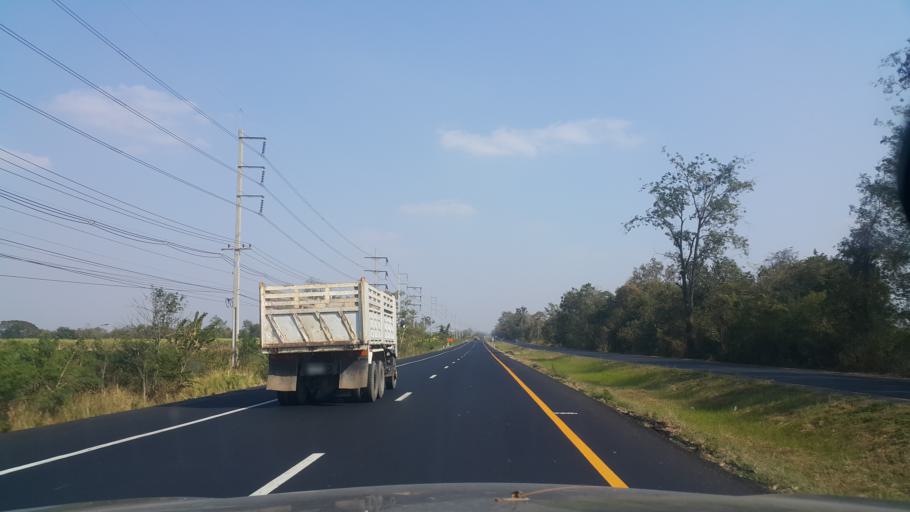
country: TH
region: Nakhon Ratchasima
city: Nong Bun Nak
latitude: 14.7267
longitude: 102.4134
